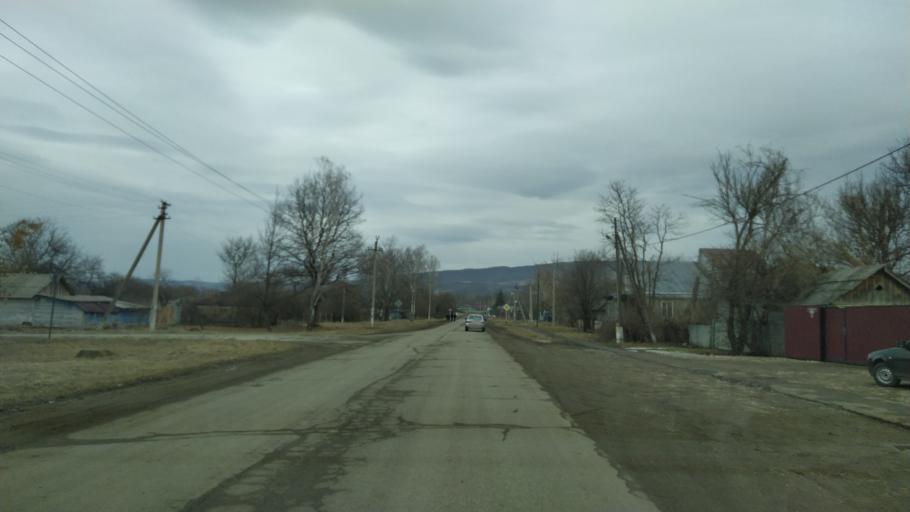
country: RU
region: Krasnodarskiy
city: Peredovaya
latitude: 44.1179
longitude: 41.4669
